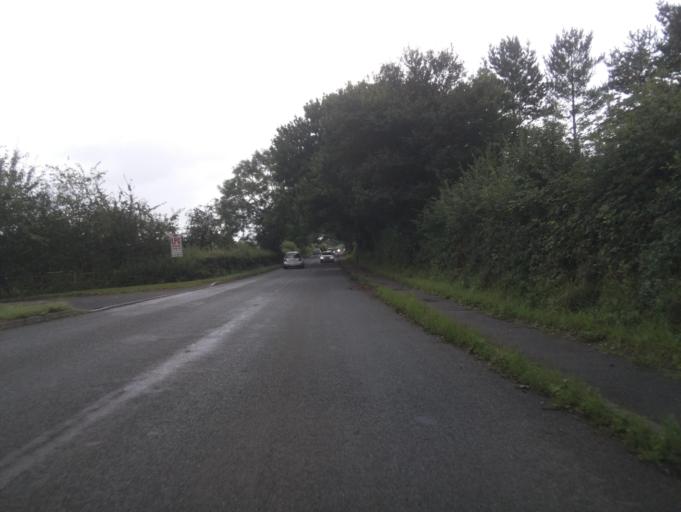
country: GB
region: England
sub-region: Solihull
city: Cheswick Green
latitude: 52.3846
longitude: -1.8222
